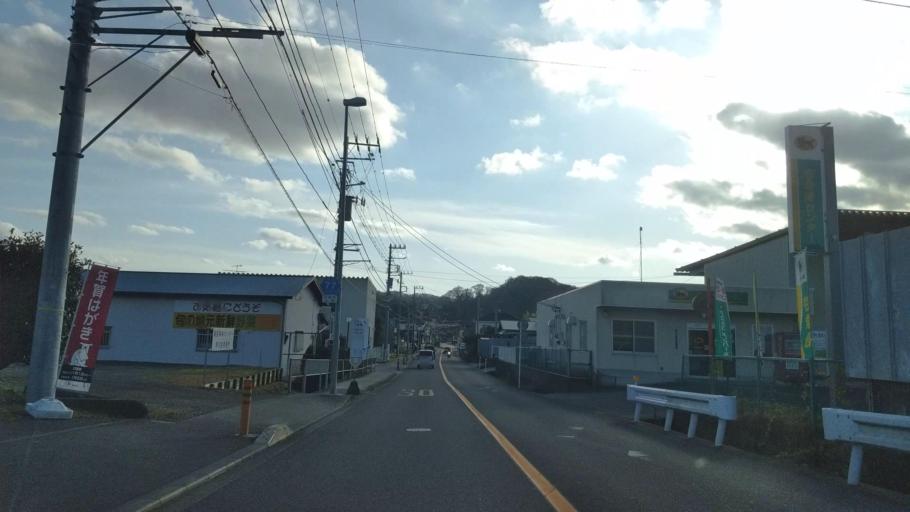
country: JP
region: Kanagawa
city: Hadano
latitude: 35.3553
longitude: 139.2695
